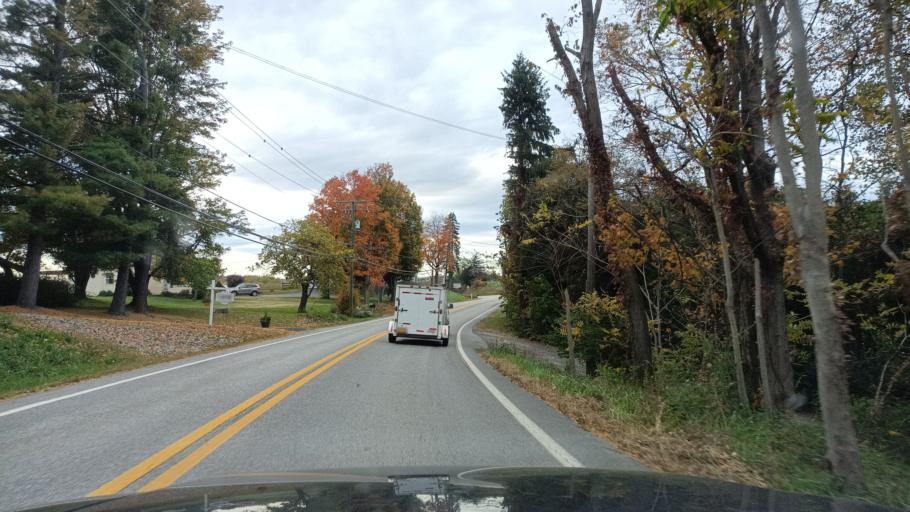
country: US
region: West Virginia
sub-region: Monongalia County
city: Morgantown
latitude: 39.5758
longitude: -79.9493
